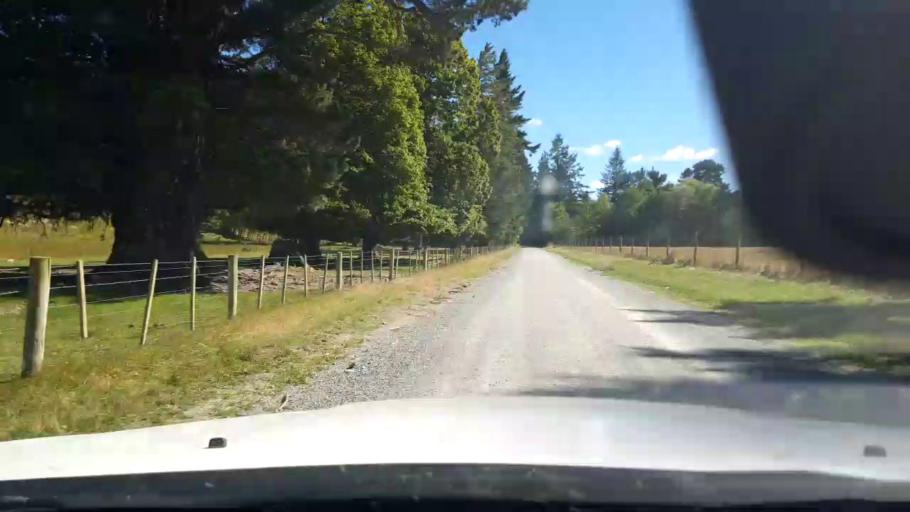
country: NZ
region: Canterbury
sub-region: Timaru District
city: Pleasant Point
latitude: -44.0275
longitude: 170.7436
